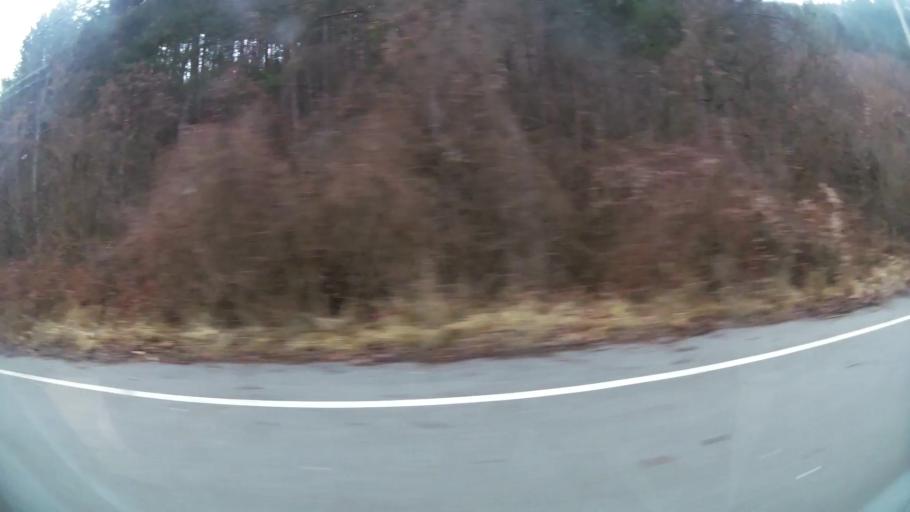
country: BG
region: Sofia-Capital
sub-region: Stolichna Obshtina
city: Sofia
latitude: 42.5854
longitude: 23.4281
